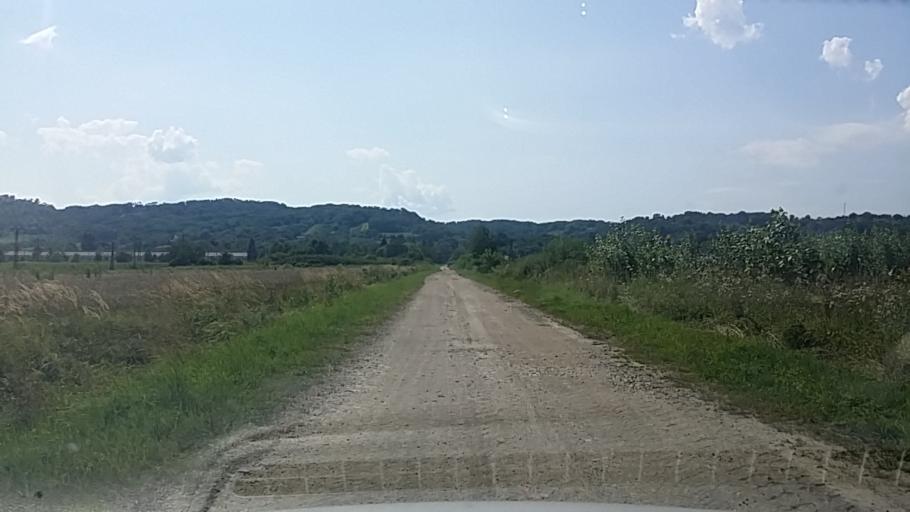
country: HU
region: Zala
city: Lenti
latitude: 46.5505
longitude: 16.5636
